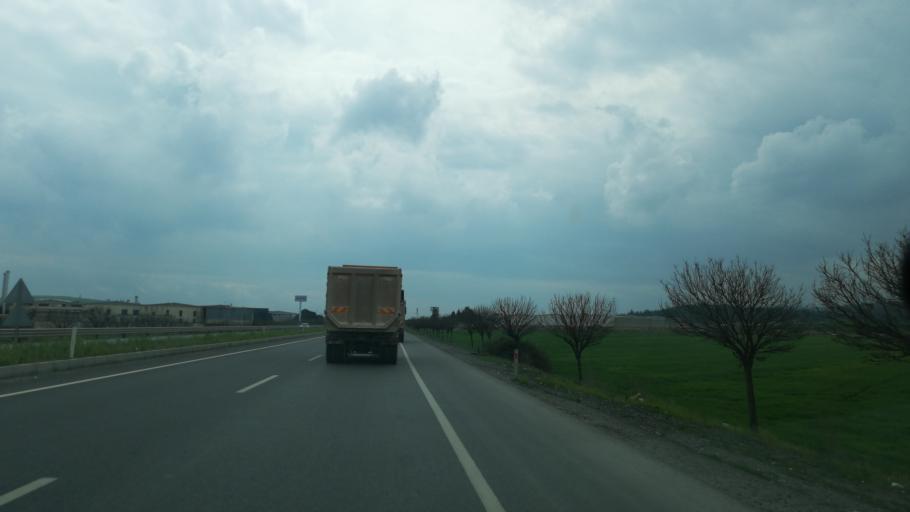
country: TR
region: Kahramanmaras
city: Turkoglu
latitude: 37.4378
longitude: 36.8860
